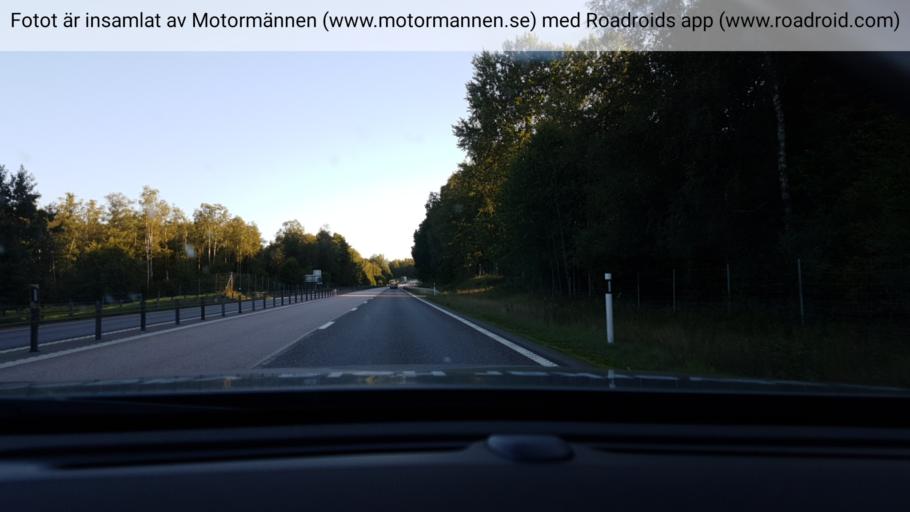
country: SE
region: Halland
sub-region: Halmstads Kommun
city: Oskarstrom
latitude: 56.8231
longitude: 12.9625
